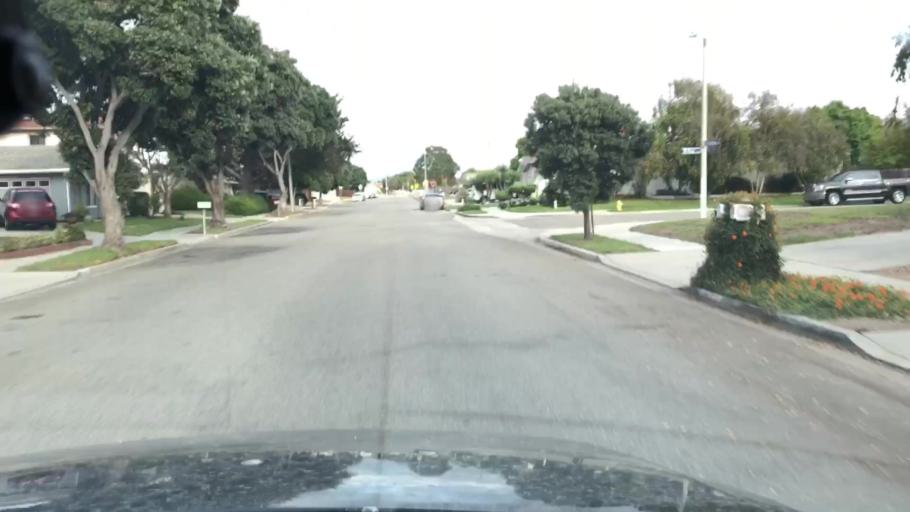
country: US
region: California
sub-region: Ventura County
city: Oxnard Shores
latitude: 34.1885
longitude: -119.2158
